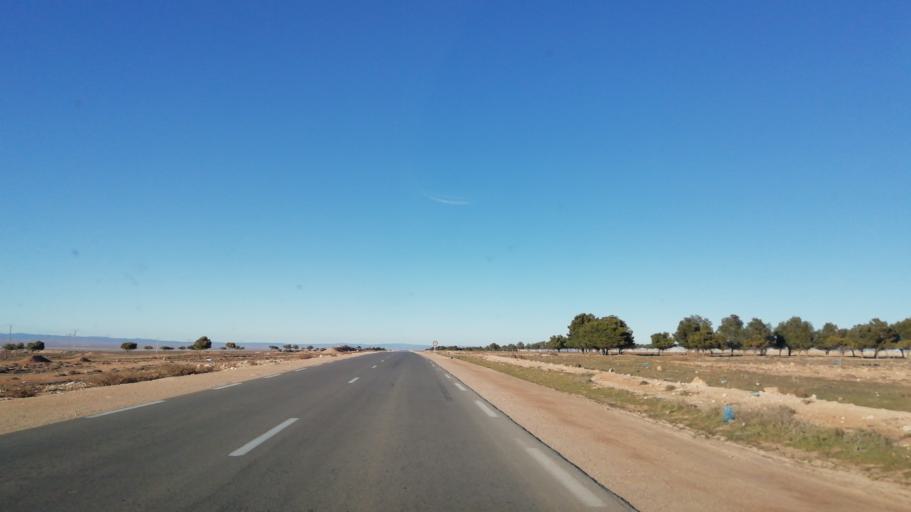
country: DZ
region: Tlemcen
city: Sebdou
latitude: 34.2785
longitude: -1.2589
